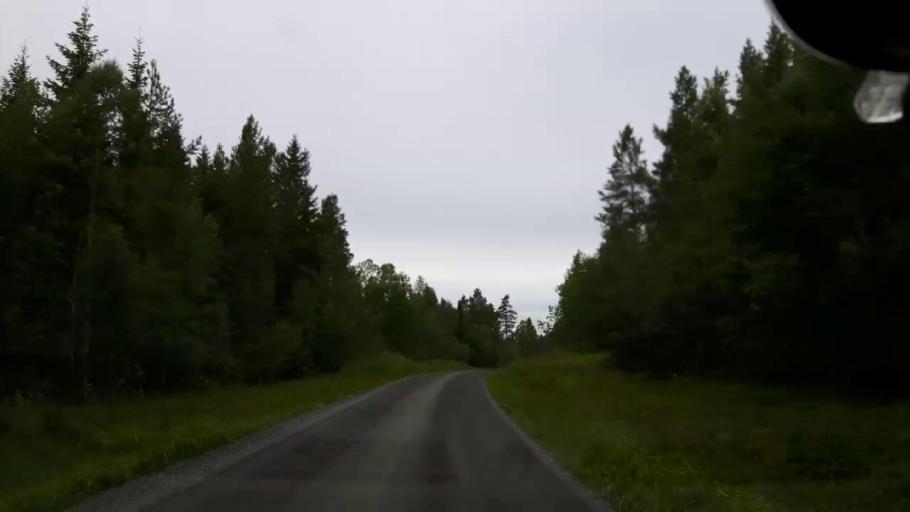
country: SE
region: Jaemtland
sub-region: Krokoms Kommun
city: Krokom
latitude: 63.2959
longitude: 14.3676
